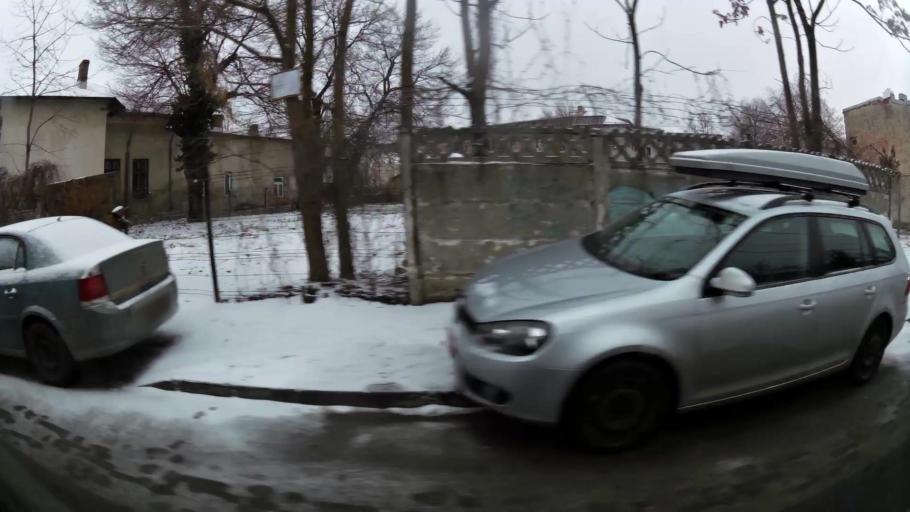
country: RO
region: Prahova
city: Ploiesti
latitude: 44.9382
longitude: 26.0312
